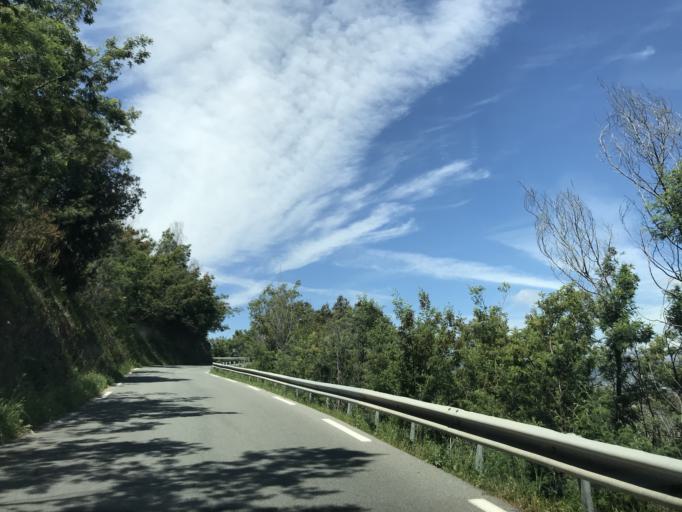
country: FR
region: Provence-Alpes-Cote d'Azur
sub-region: Departement du Var
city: Tanneron
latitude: 43.5876
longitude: 6.8842
